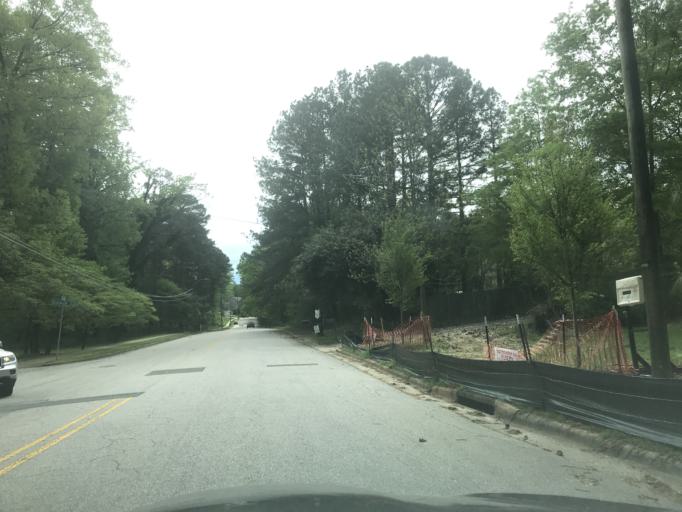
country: US
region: North Carolina
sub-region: Wake County
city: West Raleigh
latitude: 35.7825
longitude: -78.7128
